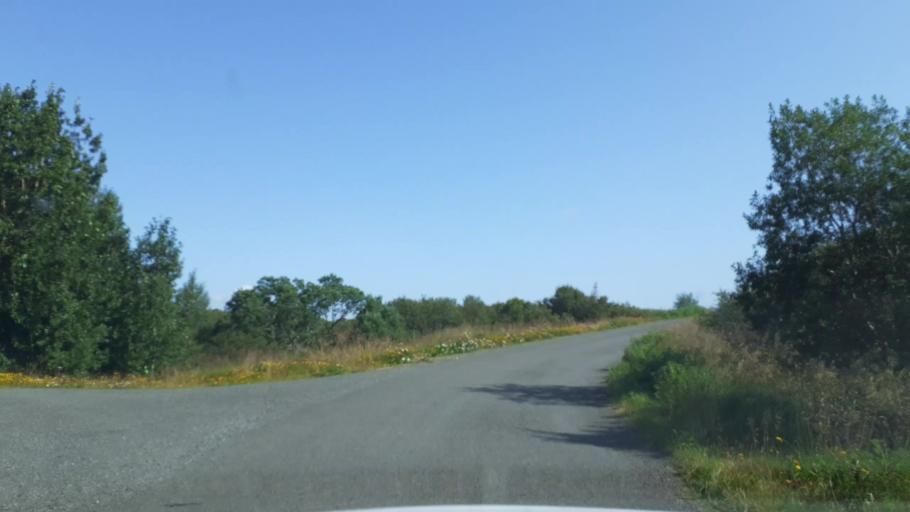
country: IS
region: West
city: Borgarnes
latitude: 64.7018
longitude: -21.6218
